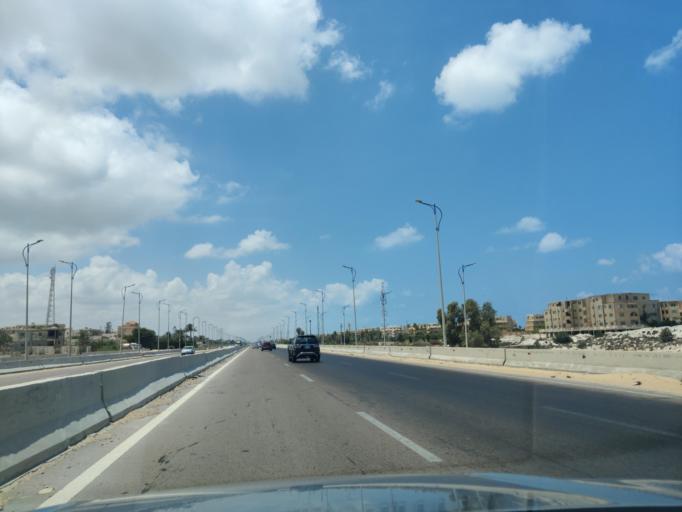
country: EG
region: Alexandria
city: Alexandria
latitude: 30.9371
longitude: 29.4922
